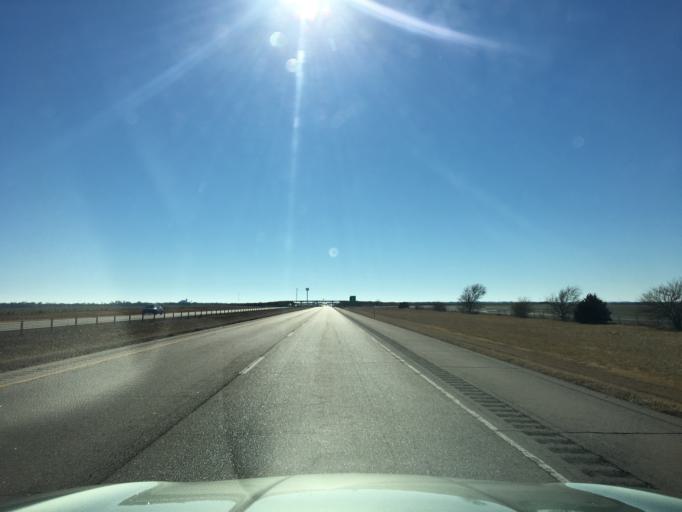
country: US
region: Oklahoma
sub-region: Kay County
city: Blackwell
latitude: 36.9618
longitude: -97.3458
